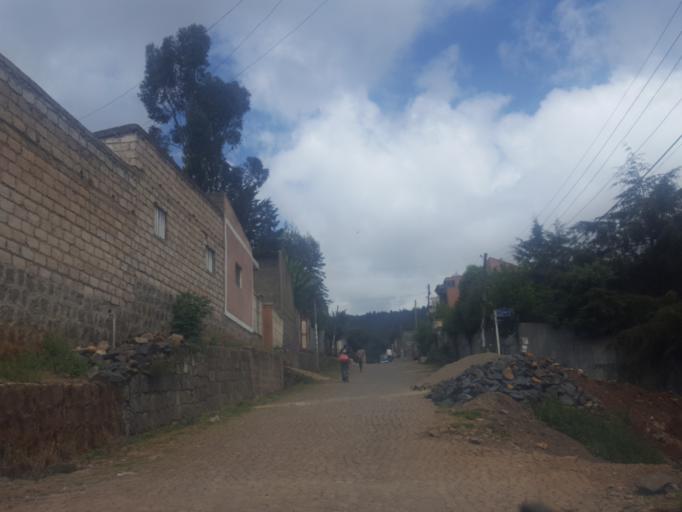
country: ET
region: Adis Abeba
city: Addis Ababa
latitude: 9.0668
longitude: 38.7368
